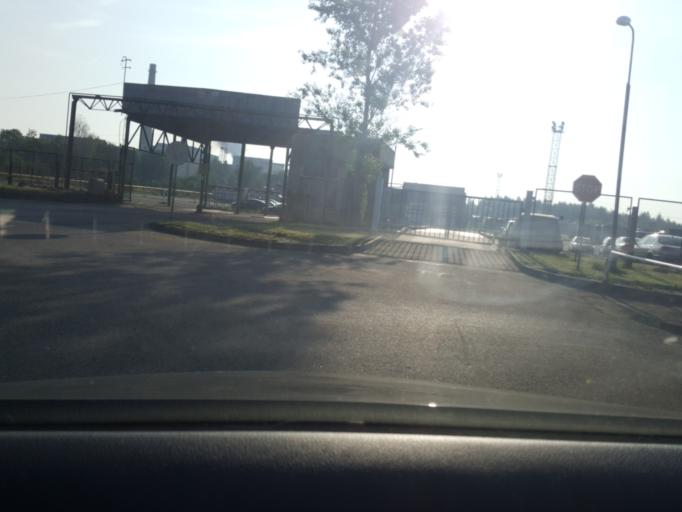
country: LT
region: Alytaus apskritis
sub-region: Alytus
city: Alytus
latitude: 54.4399
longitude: 24.0071
